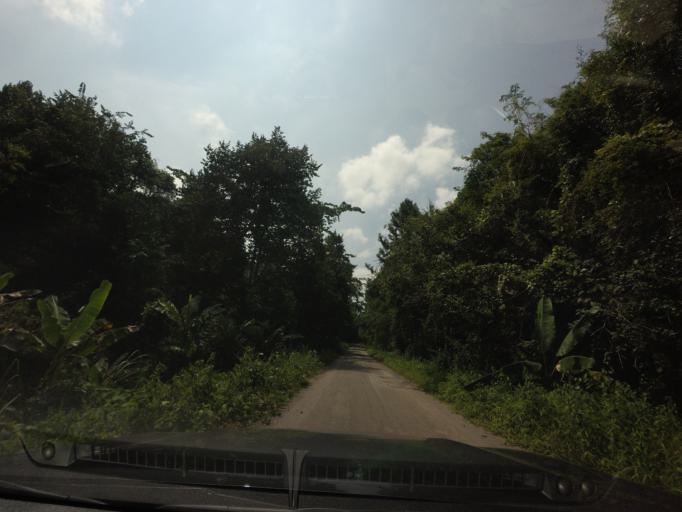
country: TH
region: Loei
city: Na Haeo
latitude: 17.4841
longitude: 100.9395
